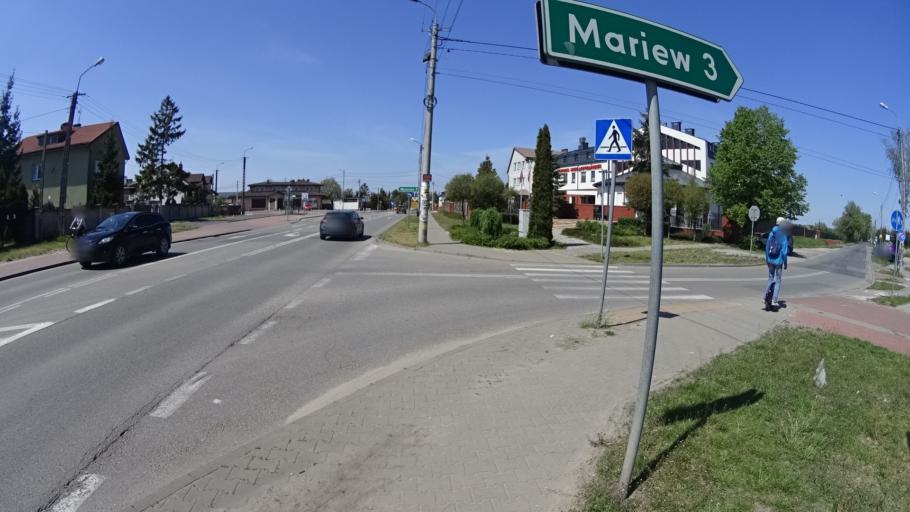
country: PL
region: Masovian Voivodeship
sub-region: Powiat warszawski zachodni
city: Truskaw
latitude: 52.2522
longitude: 20.7353
